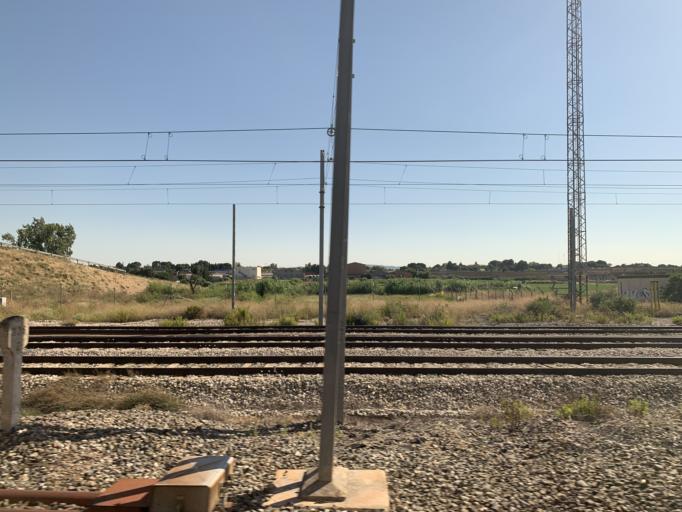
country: ES
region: Aragon
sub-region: Provincia de Zaragoza
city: Oliver-Valdefierro, Oliver, Valdefierro
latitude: 41.6757
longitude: -0.9406
